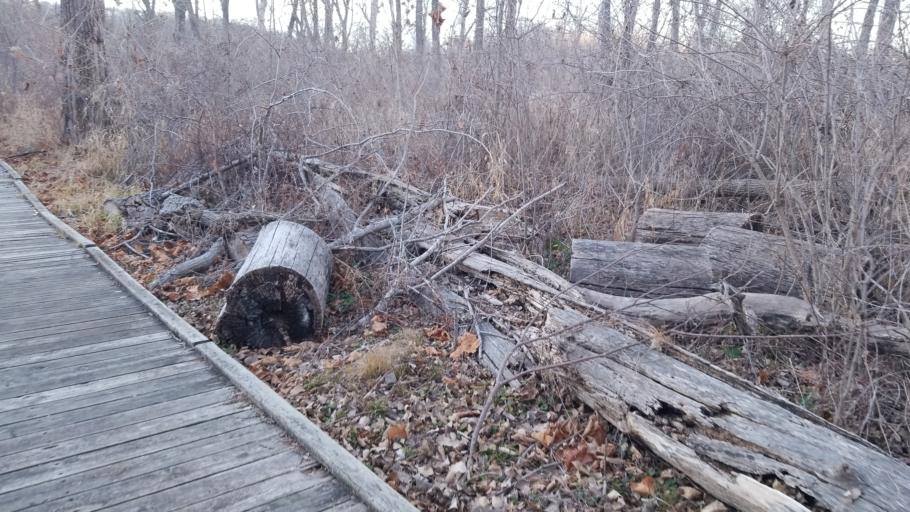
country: US
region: Nebraska
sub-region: Sarpy County
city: Bellevue
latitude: 41.1732
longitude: -95.8878
